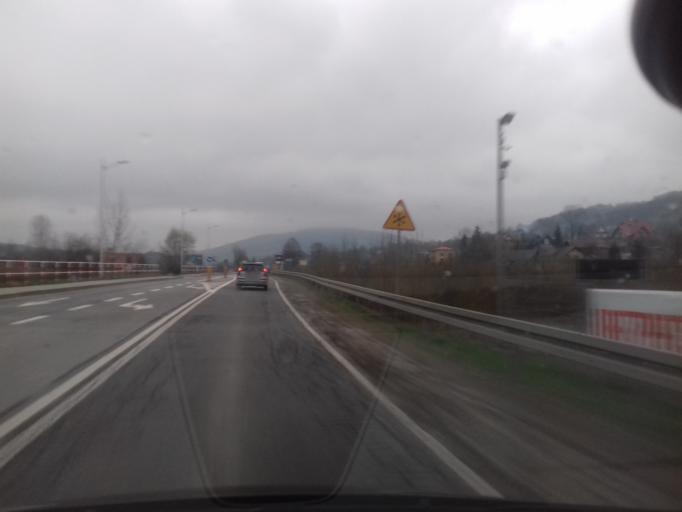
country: PL
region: Lesser Poland Voivodeship
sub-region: Powiat limanowski
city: Mszana Dolna
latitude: 49.6848
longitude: 20.0516
